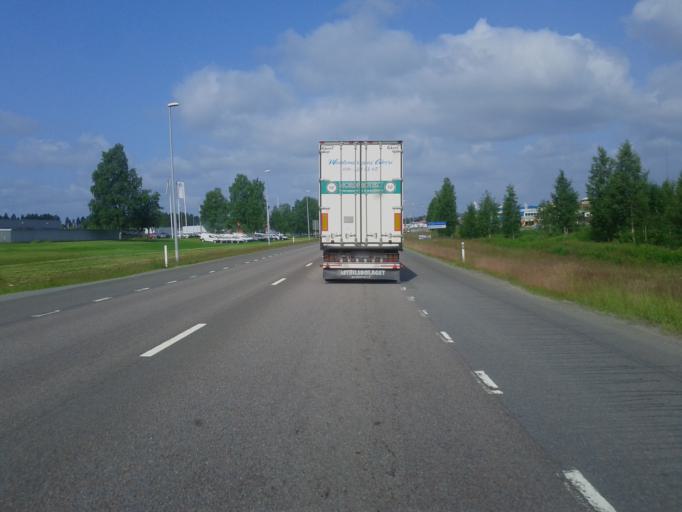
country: SE
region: Vaesterbotten
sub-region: Skelleftea Kommun
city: Skelleftea
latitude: 64.7329
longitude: 20.9713
